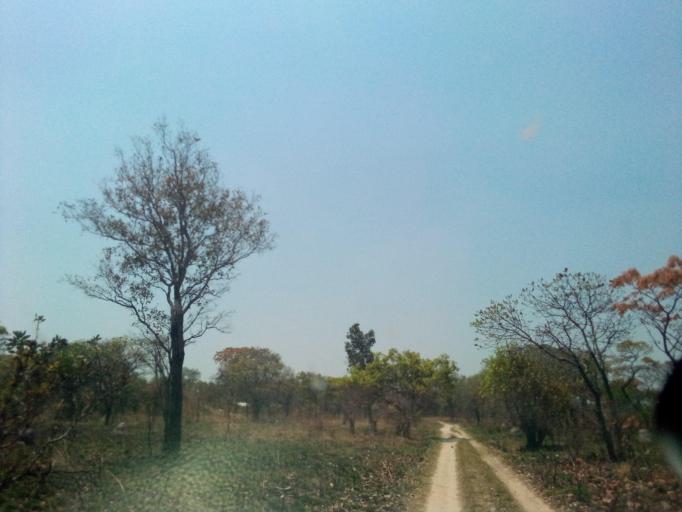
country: ZM
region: Copperbelt
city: Kataba
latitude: -12.2397
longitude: 30.4034
